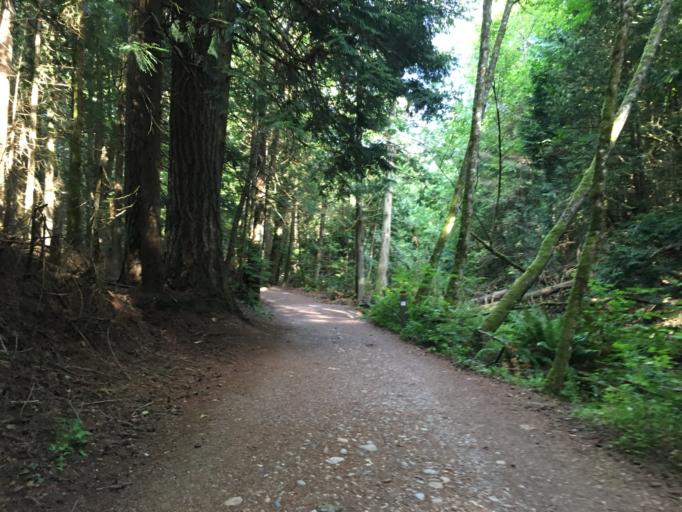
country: US
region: Washington
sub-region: Whatcom County
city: Bellingham
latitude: 48.7010
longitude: -122.4586
